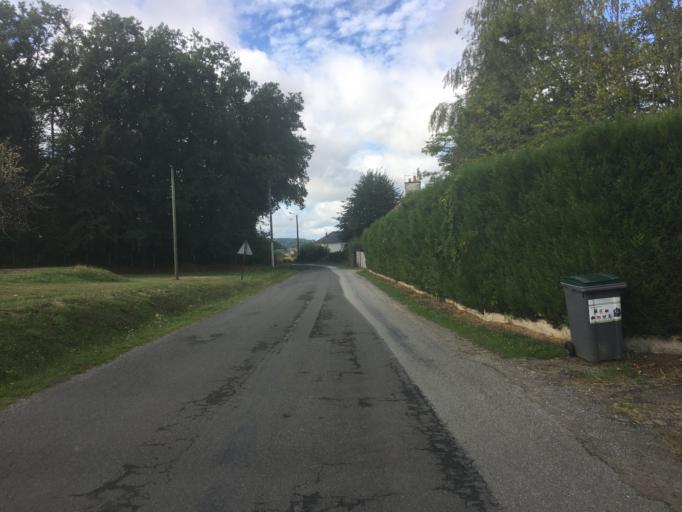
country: FR
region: Limousin
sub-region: Departement de la Correze
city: Bort-les-Orgues
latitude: 45.4152
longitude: 2.4377
